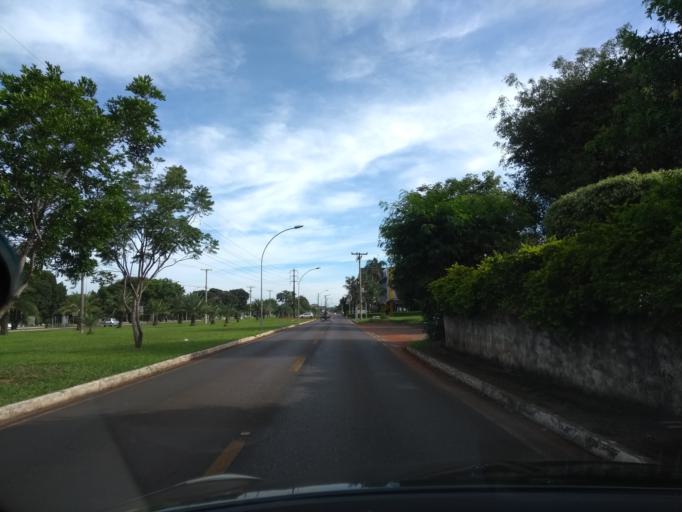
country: BR
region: Federal District
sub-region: Brasilia
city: Brasilia
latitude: -15.7885
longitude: -47.9316
